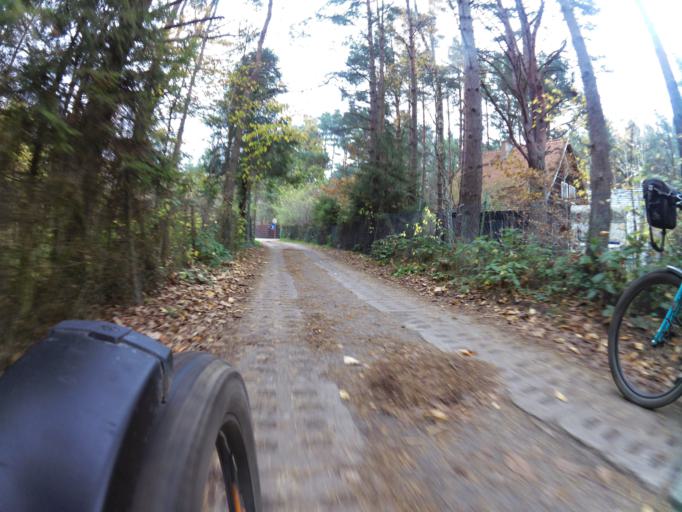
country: PL
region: Pomeranian Voivodeship
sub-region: Powiat pucki
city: Wierzchucino
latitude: 54.8292
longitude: 18.0815
